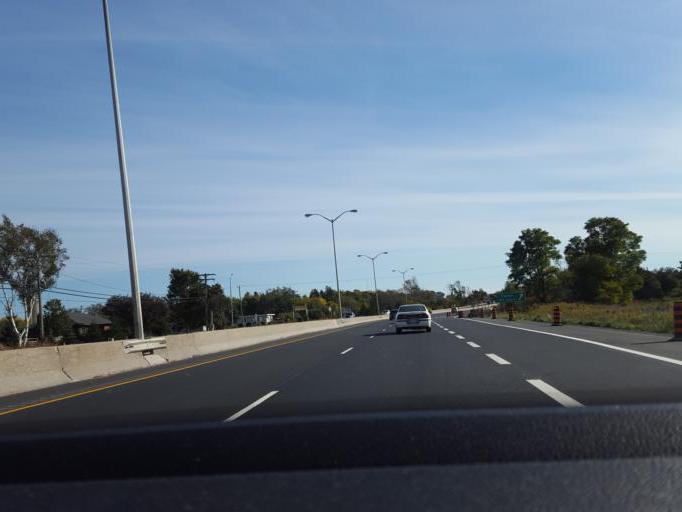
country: CA
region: Ontario
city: Oshawa
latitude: 43.9535
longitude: -78.6071
